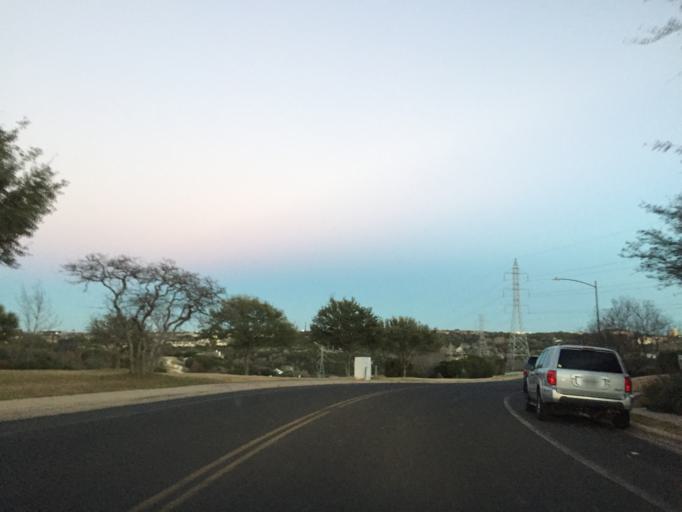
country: US
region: Texas
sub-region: Williamson County
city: Jollyville
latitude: 30.4020
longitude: -97.7667
